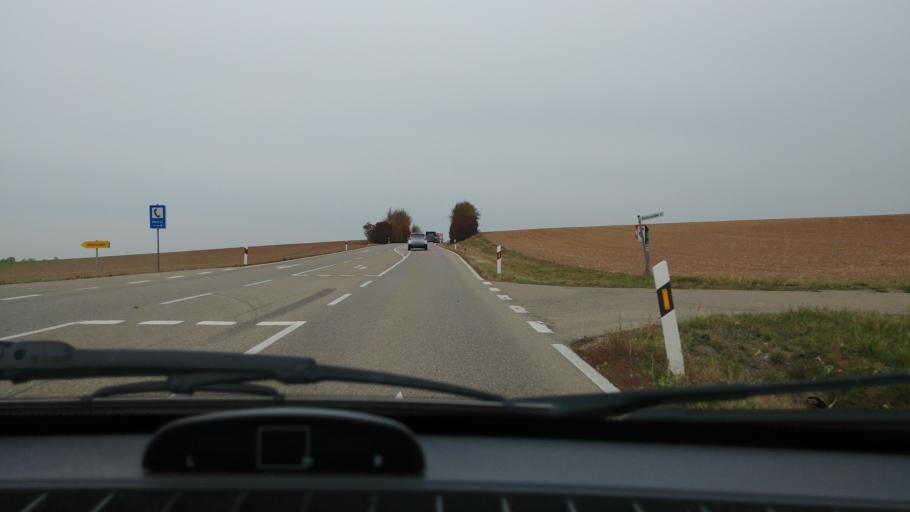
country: DE
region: Baden-Wuerttemberg
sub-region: Regierungsbezirk Stuttgart
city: Wallhausen
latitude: 49.2330
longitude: 10.0432
